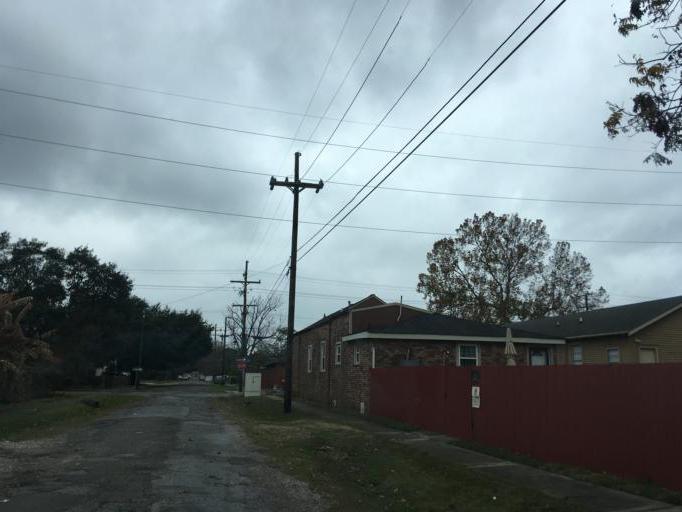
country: US
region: Louisiana
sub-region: Orleans Parish
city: New Orleans
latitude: 29.9939
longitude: -90.0596
